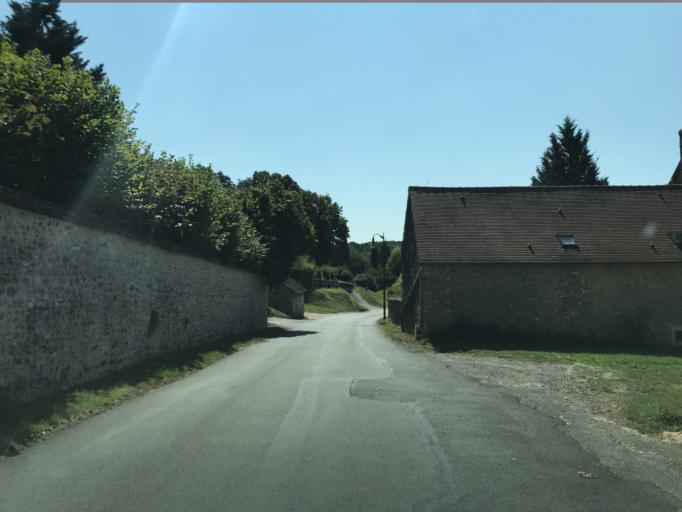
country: FR
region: Haute-Normandie
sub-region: Departement de l'Eure
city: La Chapelle-Reanville
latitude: 49.0963
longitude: 1.3786
